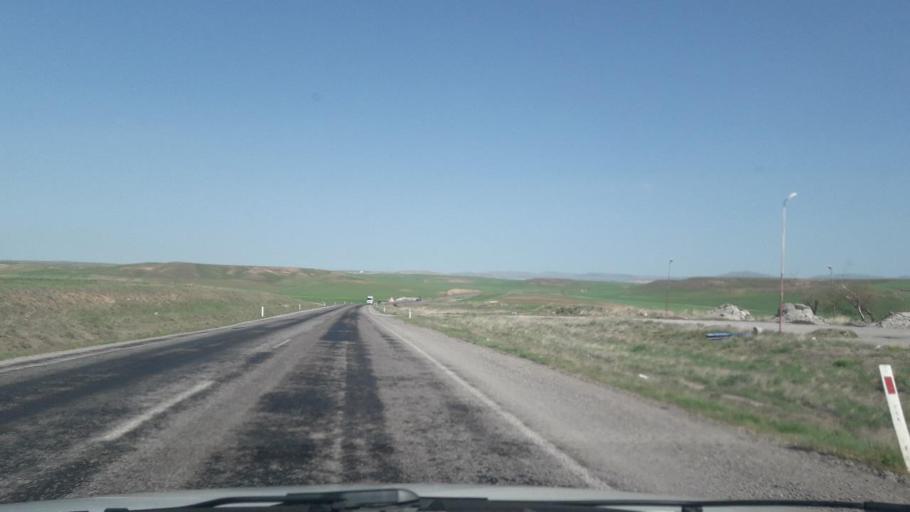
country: TR
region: Sivas
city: Kangal
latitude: 39.1873
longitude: 37.4286
